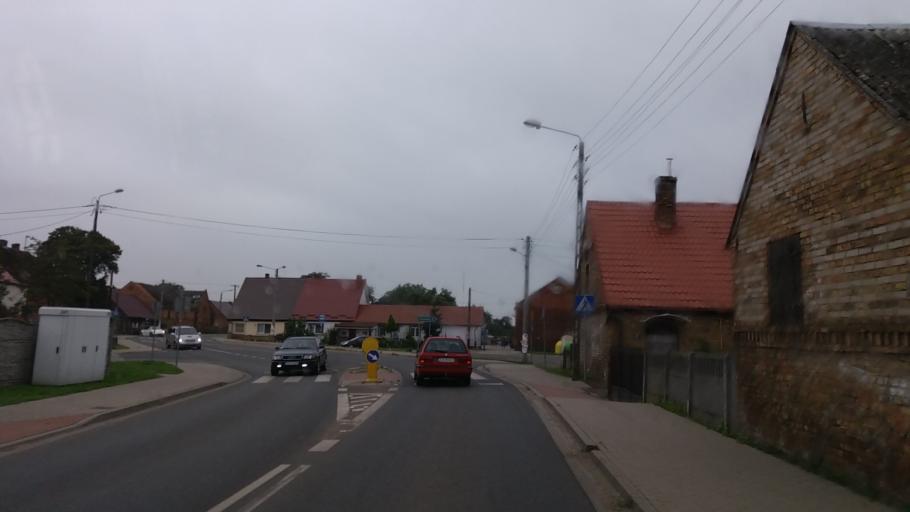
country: PL
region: West Pomeranian Voivodeship
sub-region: Powiat choszczenski
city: Choszczno
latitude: 53.1315
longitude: 15.3768
